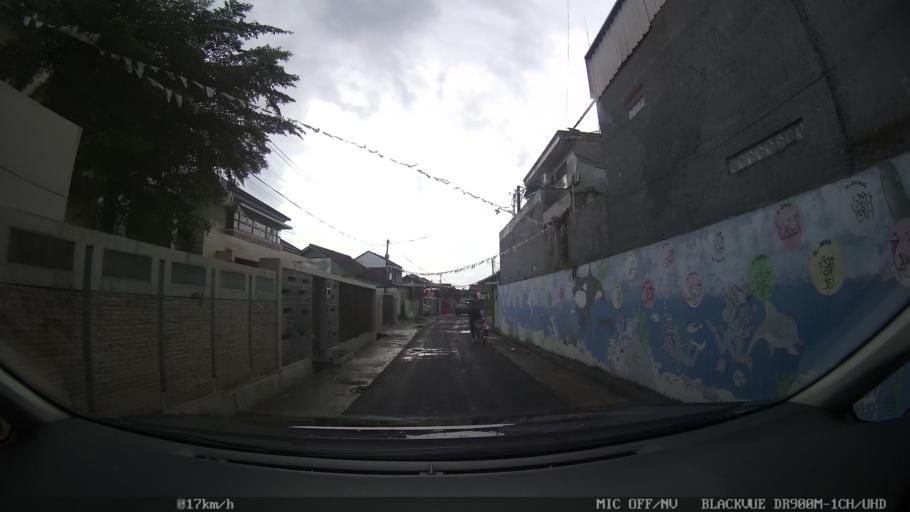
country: ID
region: Lampung
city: Kedaton
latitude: -5.3975
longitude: 105.2852
